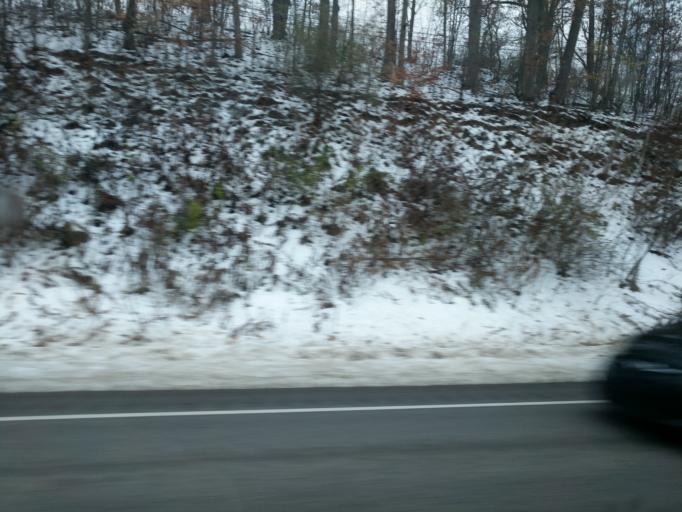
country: US
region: Pennsylvania
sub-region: Tioga County
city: Wellsboro
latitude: 41.8047
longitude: -77.2931
